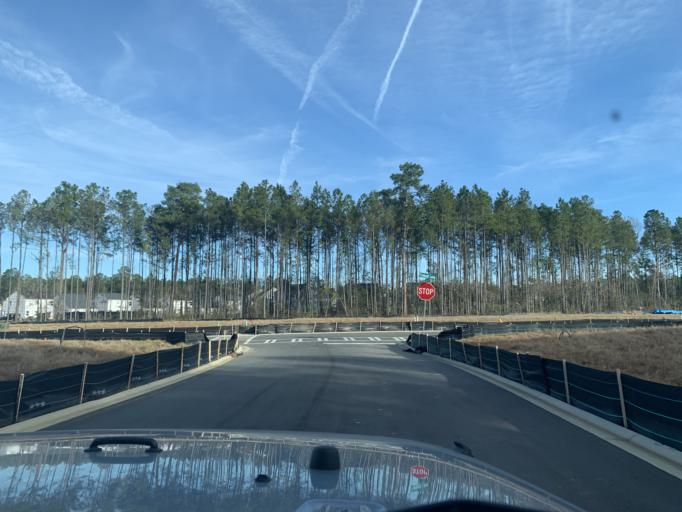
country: US
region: Georgia
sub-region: Chatham County
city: Pooler
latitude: 32.0659
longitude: -81.2558
